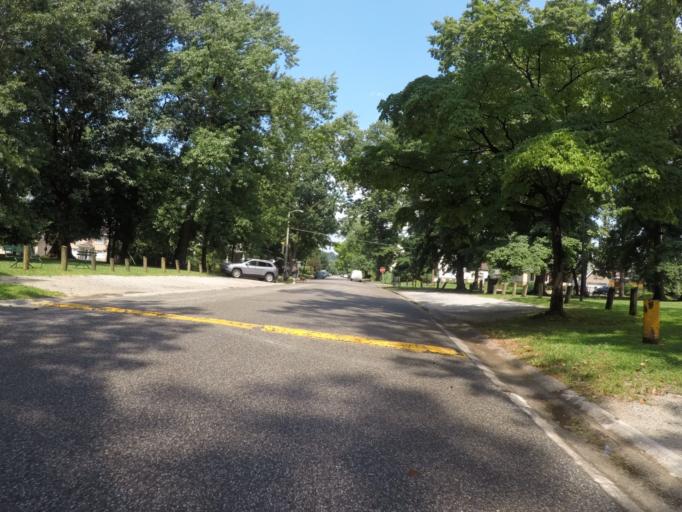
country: US
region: Kentucky
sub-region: Boyd County
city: Ashland
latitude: 38.4741
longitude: -82.6409
